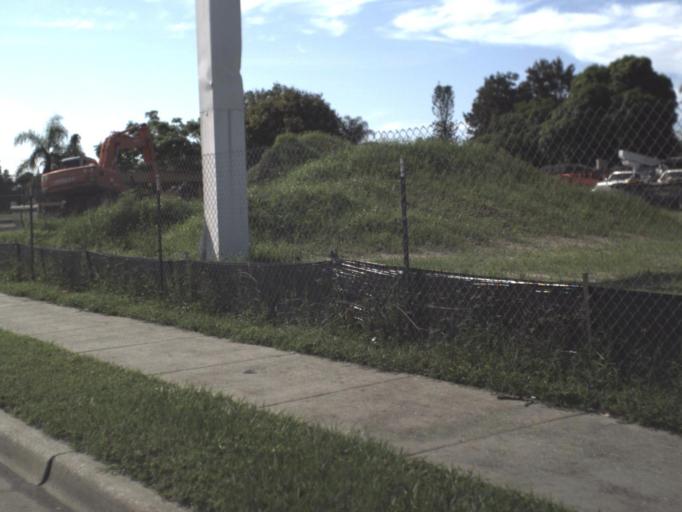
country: US
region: Florida
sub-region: Sarasota County
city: Gulf Gate Estates
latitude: 27.2625
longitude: -82.5247
